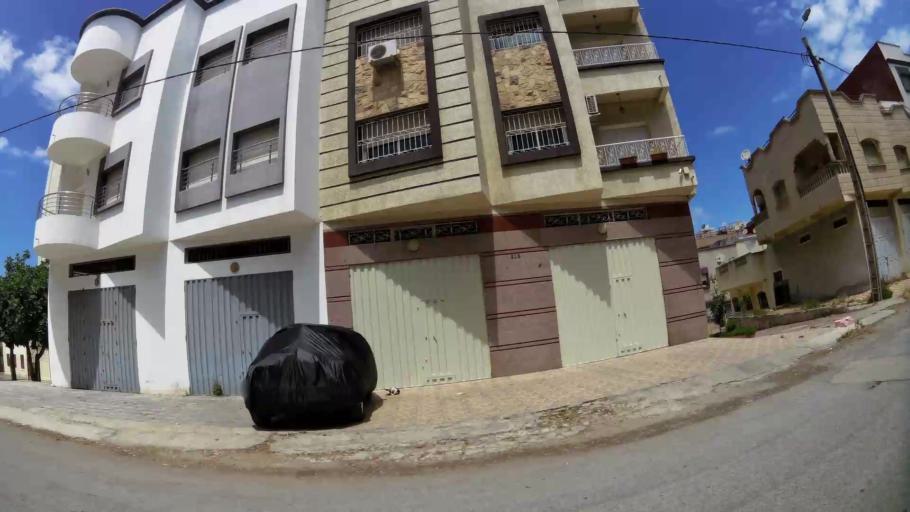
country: MA
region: Gharb-Chrarda-Beni Hssen
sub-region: Kenitra Province
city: Kenitra
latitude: 34.2718
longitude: -6.5989
